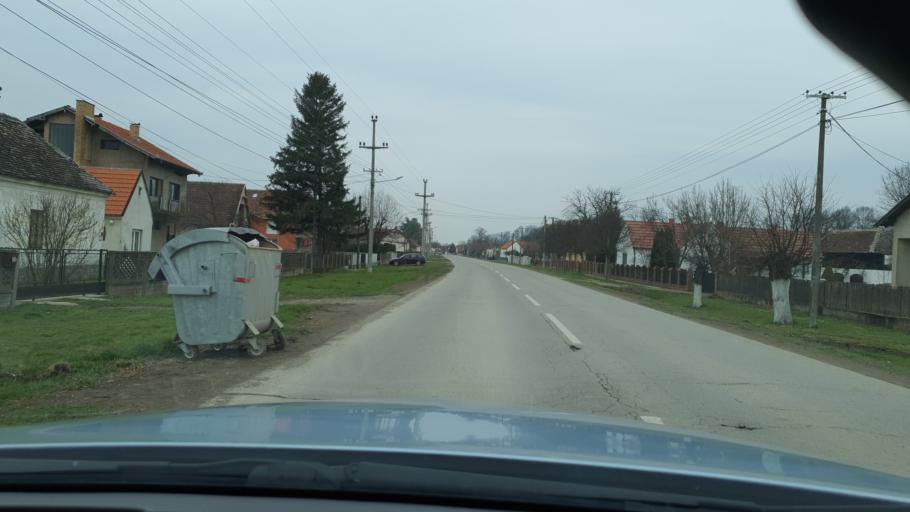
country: RS
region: Central Serbia
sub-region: Macvanski Okrug
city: Bogatic
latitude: 44.8329
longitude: 19.4982
